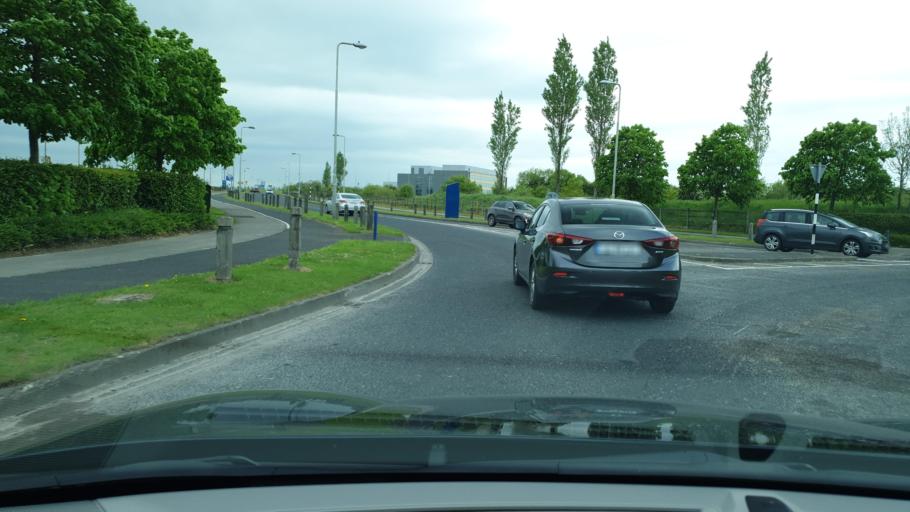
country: IE
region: Leinster
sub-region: Kildare
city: Sallins
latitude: 53.2337
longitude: -6.6774
